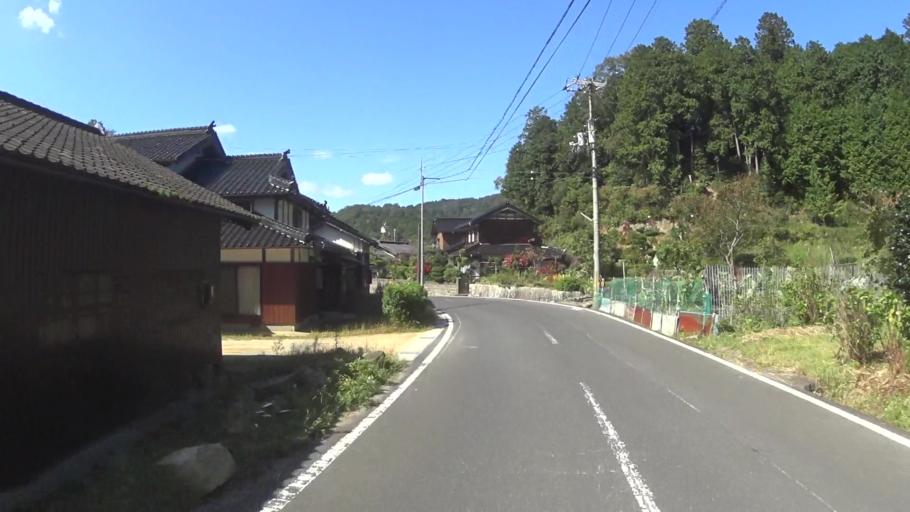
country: JP
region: Hyogo
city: Toyooka
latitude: 35.5950
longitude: 134.9473
